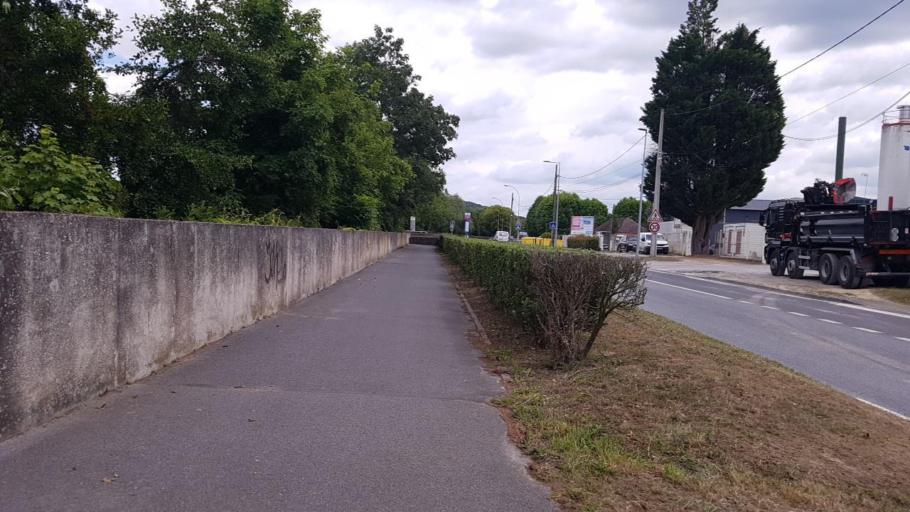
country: FR
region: Picardie
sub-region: Departement de l'Oise
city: Compiegne
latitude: 49.4287
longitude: 2.8373
